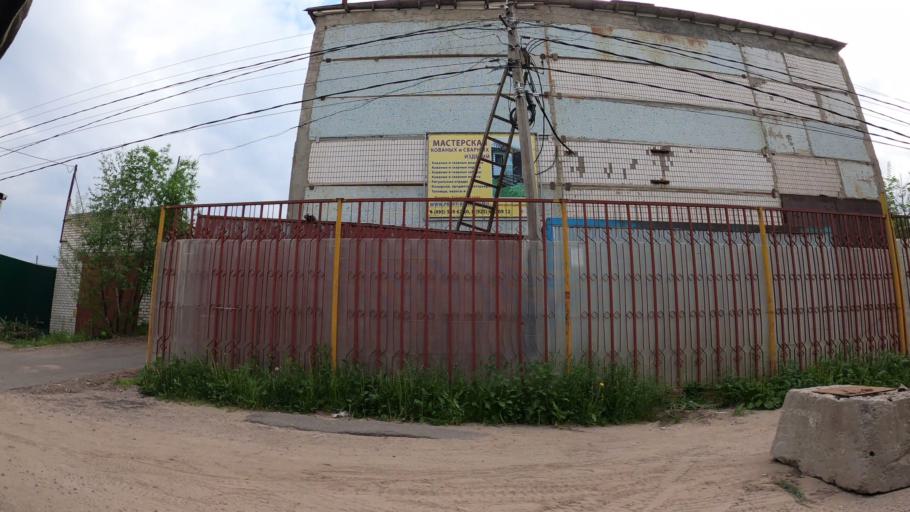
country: RU
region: Moskovskaya
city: Ivanteyevka
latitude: 55.9588
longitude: 37.9234
